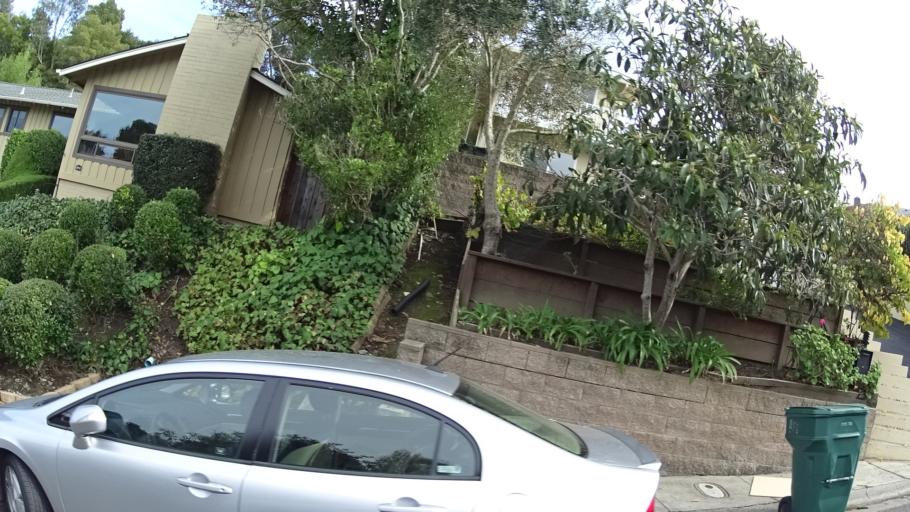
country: US
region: California
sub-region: San Mateo County
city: Hillsborough
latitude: 37.5734
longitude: -122.3842
